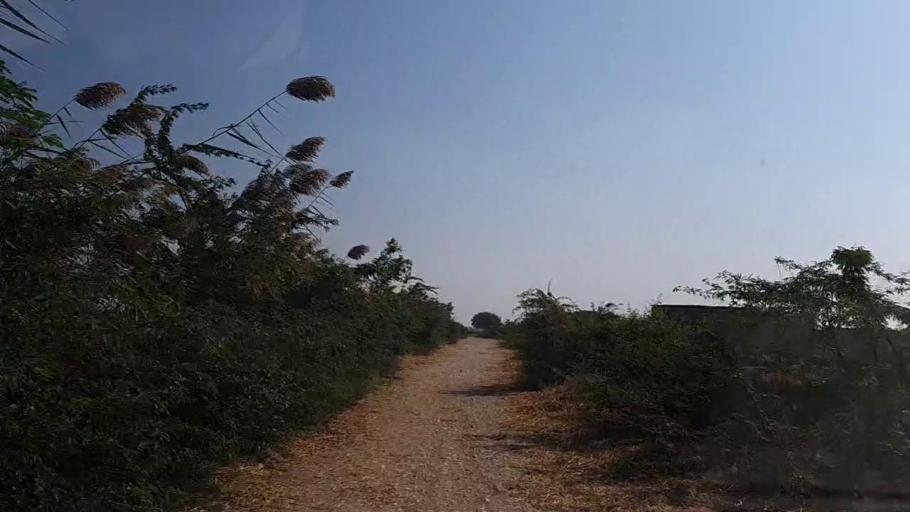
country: PK
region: Sindh
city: Thatta
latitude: 24.7667
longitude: 67.9425
